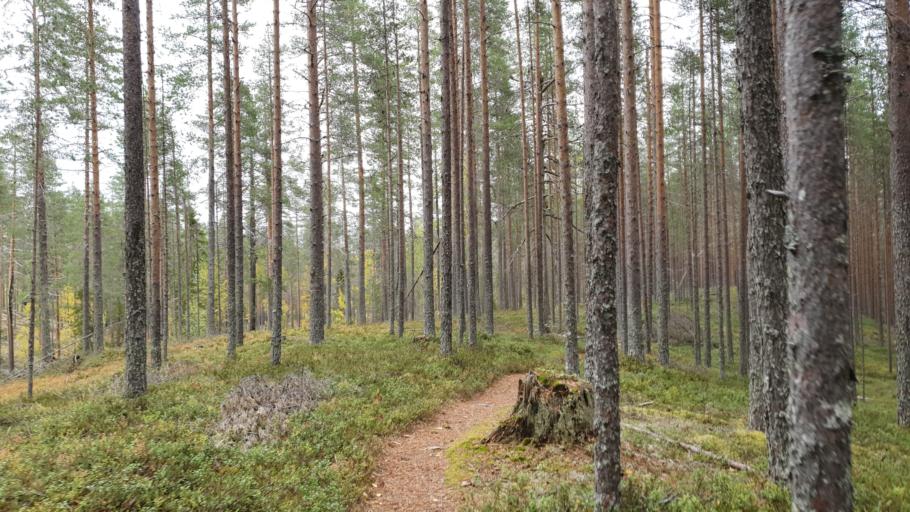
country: FI
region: Kainuu
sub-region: Kehys-Kainuu
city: Kuhmo
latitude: 64.2932
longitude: 29.3406
